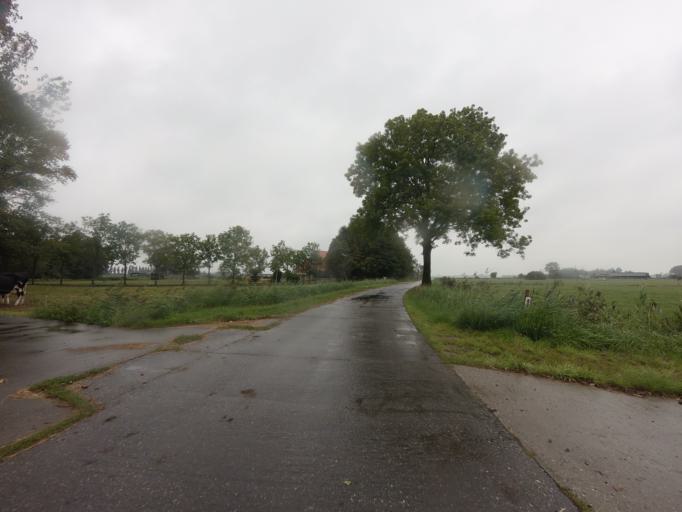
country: NL
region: Friesland
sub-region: Gemeente Boarnsterhim
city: Nes
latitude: 53.0279
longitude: 5.8651
